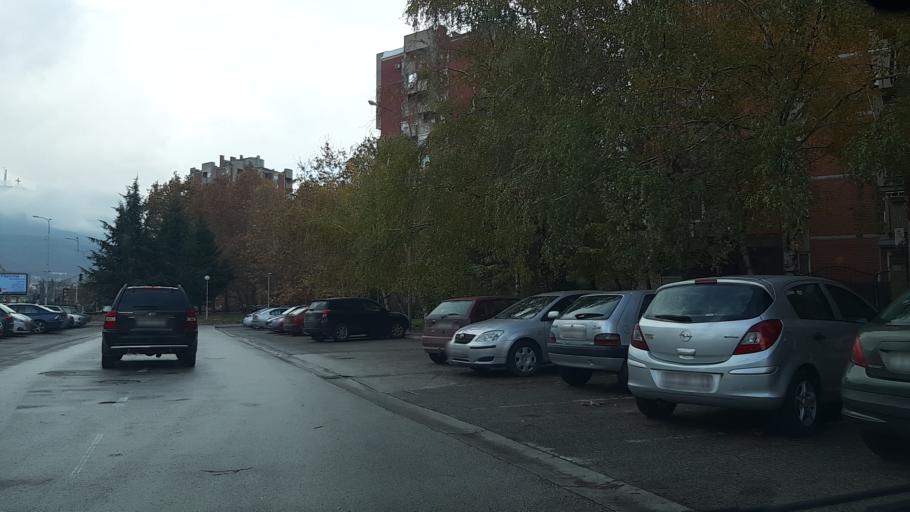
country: MK
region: Karpos
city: Skopje
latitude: 41.9892
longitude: 21.4563
